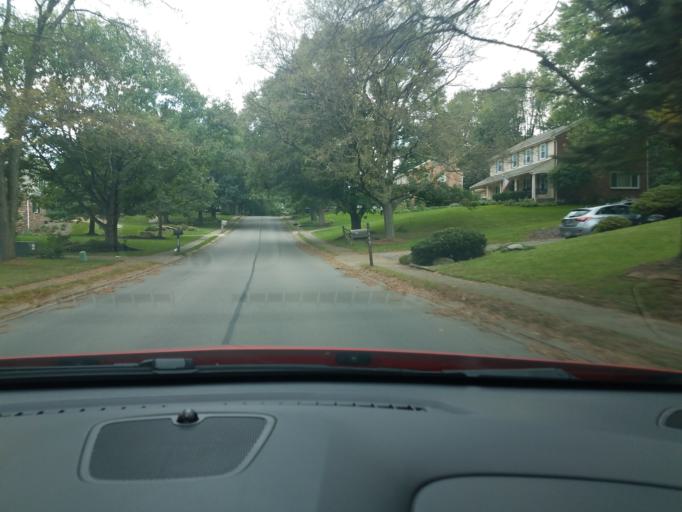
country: US
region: Pennsylvania
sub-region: Allegheny County
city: Franklin Park
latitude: 40.5670
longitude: -80.0756
